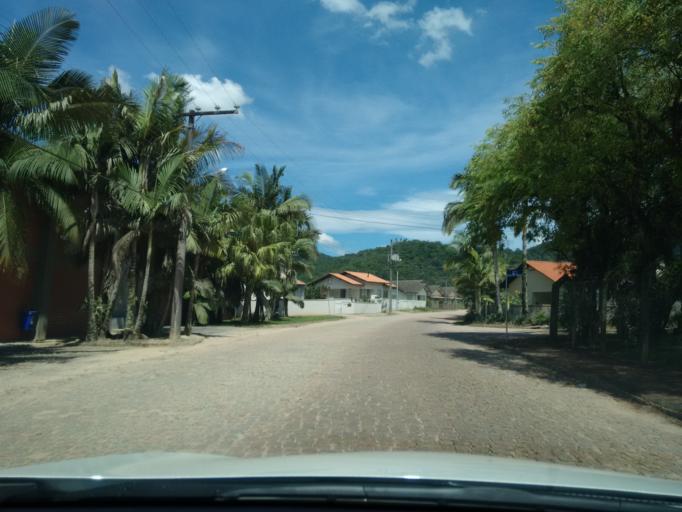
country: BR
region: Santa Catarina
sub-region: Pomerode
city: Pomerode
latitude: -26.7212
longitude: -49.1485
